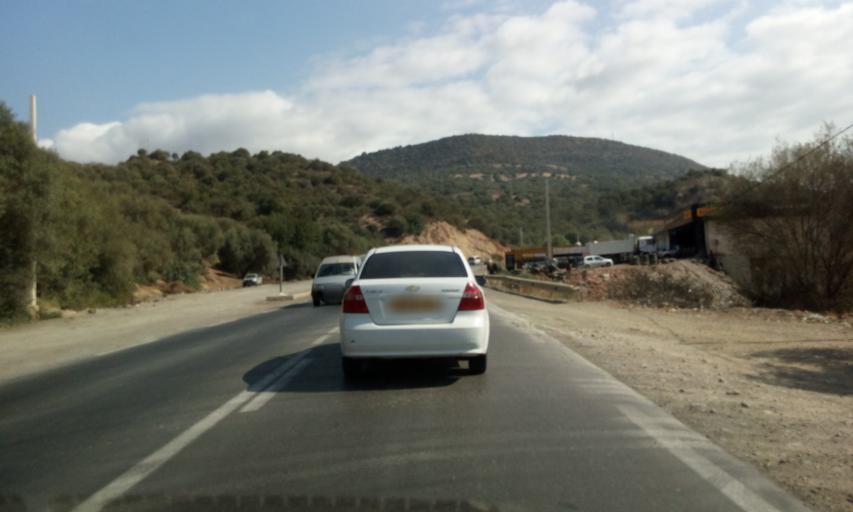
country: DZ
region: Bejaia
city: el hed
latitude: 36.6527
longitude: 4.7978
